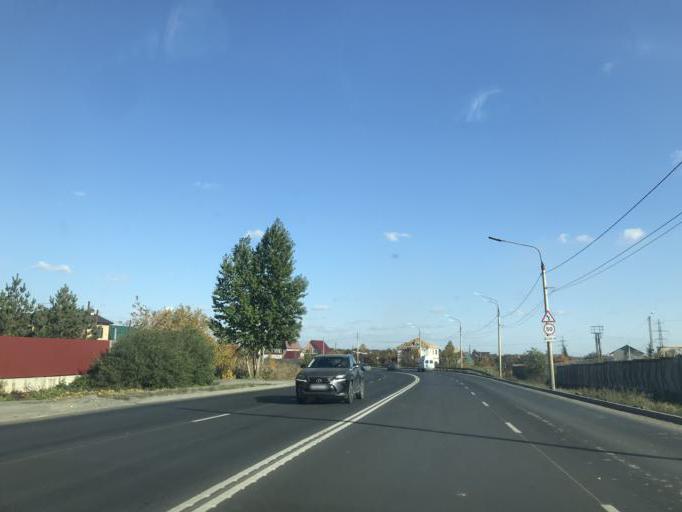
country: RU
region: Chelyabinsk
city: Roshchino
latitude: 55.2351
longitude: 61.3151
